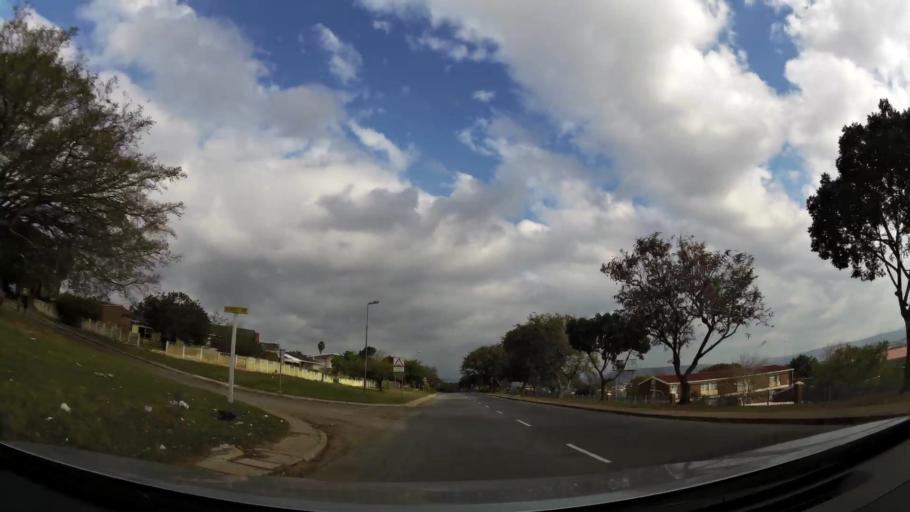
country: ZA
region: Eastern Cape
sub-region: Nelson Mandela Bay Metropolitan Municipality
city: Uitenhage
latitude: -33.7389
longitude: 25.4043
